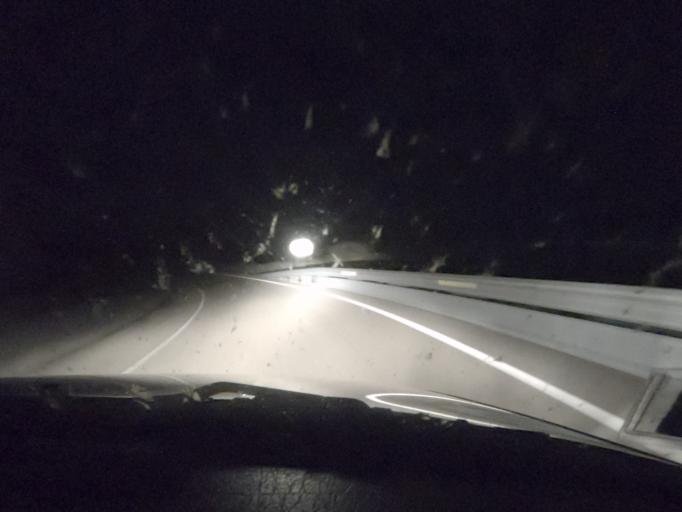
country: ES
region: Extremadura
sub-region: Provincia de Caceres
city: Acebo
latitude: 40.2392
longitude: -6.6858
